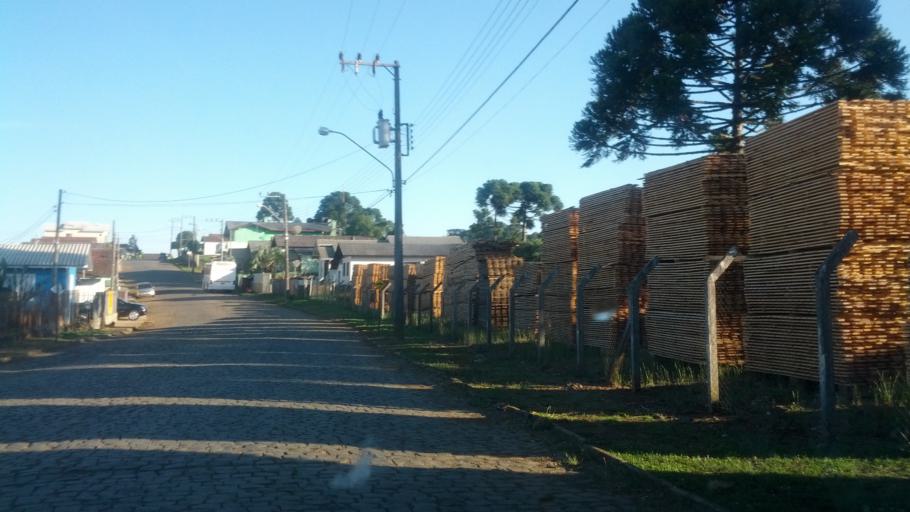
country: BR
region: Rio Grande do Sul
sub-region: Vacaria
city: Estrela
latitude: -27.9022
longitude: -50.7560
